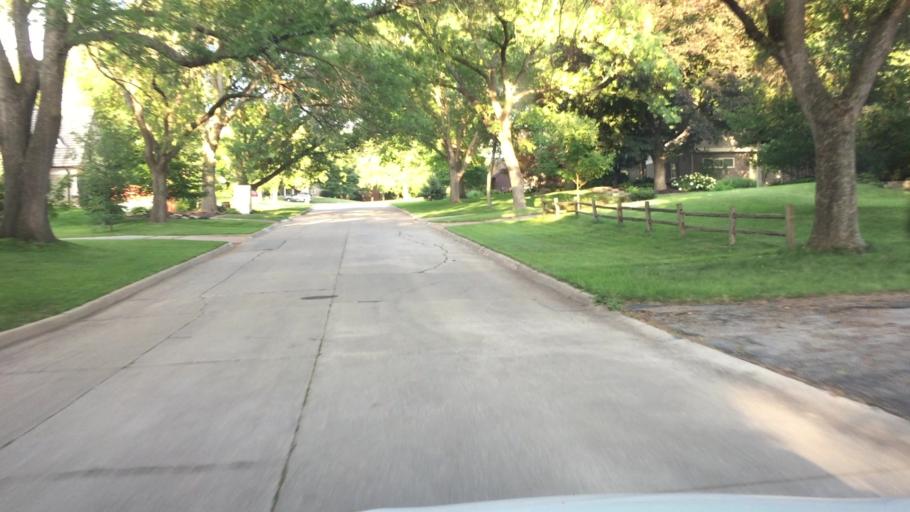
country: US
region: Iowa
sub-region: Johnson County
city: Iowa City
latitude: 41.6624
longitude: -91.5071
